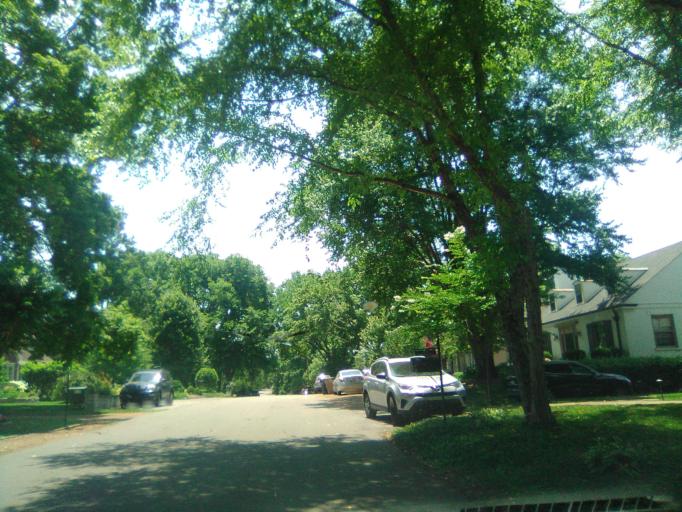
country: US
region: Tennessee
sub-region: Davidson County
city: Belle Meade
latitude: 36.1341
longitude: -86.8392
